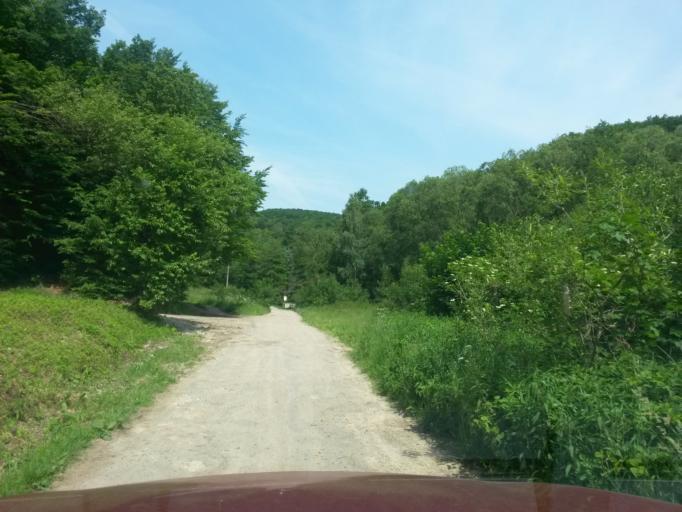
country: SK
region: Kosicky
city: Kosice
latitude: 48.7368
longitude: 21.1182
